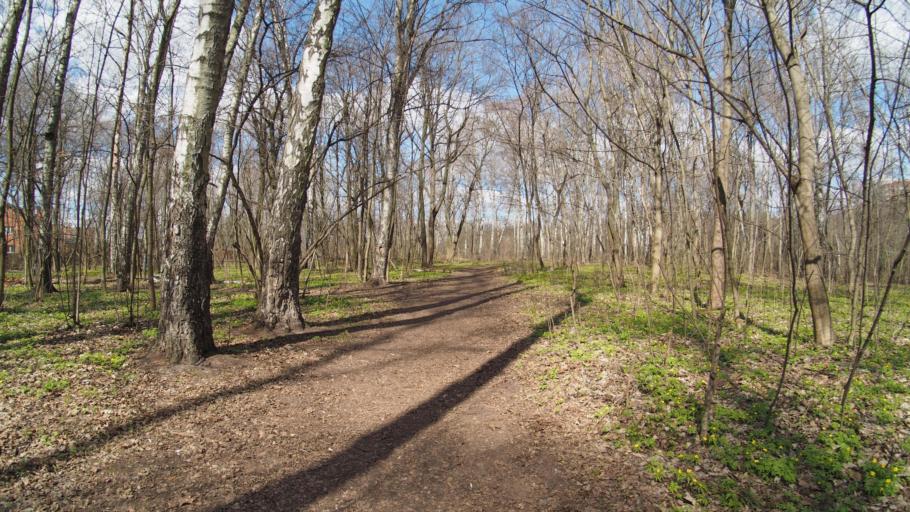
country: RU
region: Moskovskaya
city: Malyshevo
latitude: 55.5426
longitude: 38.3027
